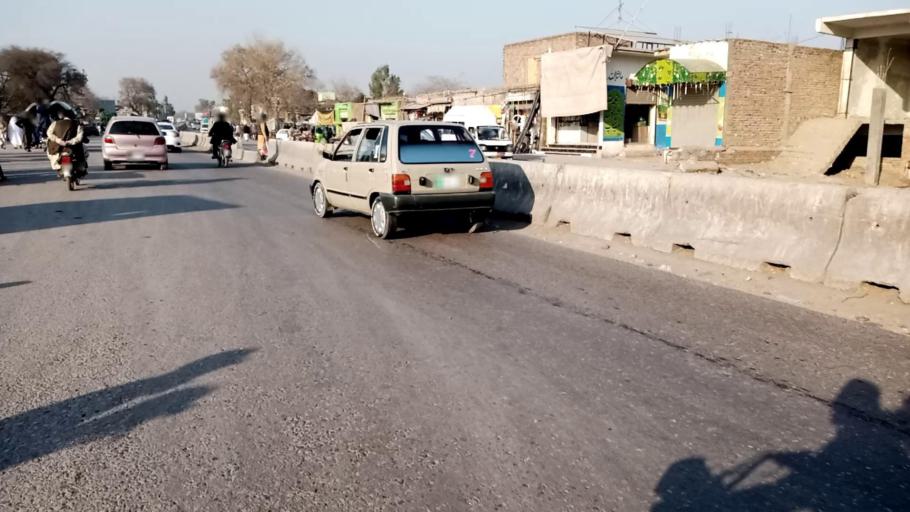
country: PK
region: Khyber Pakhtunkhwa
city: Peshawar
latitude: 33.9390
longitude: 71.5554
